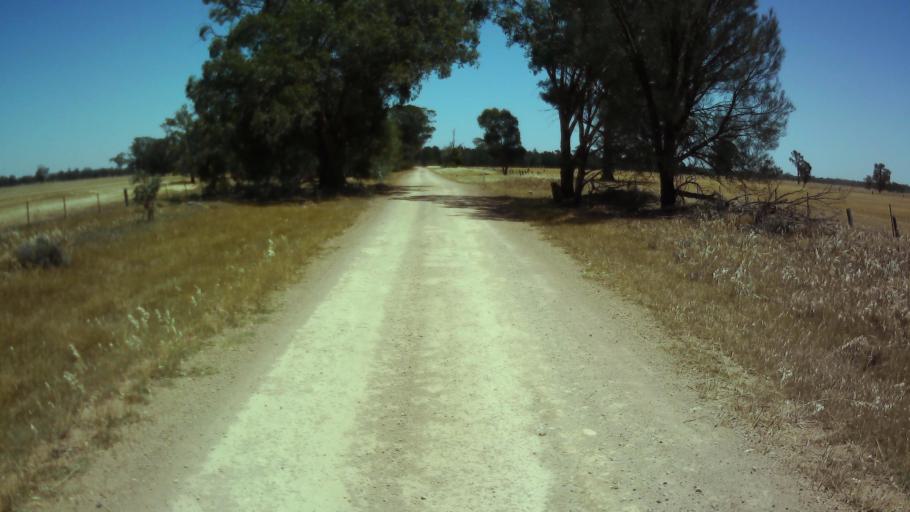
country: AU
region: New South Wales
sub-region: Weddin
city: Grenfell
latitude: -33.9911
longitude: 147.9473
